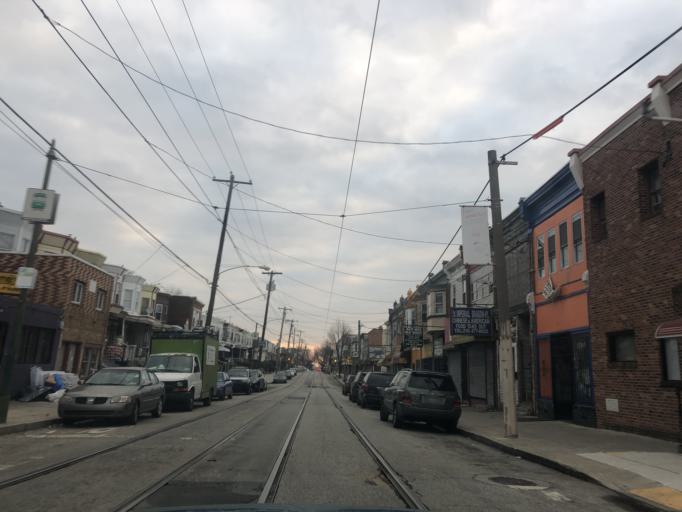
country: US
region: Pennsylvania
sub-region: Delaware County
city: Millbourne
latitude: 39.9756
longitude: -75.2436
